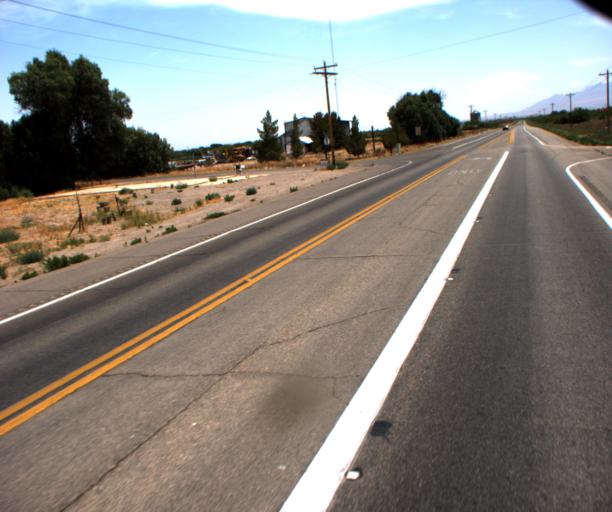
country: US
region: Arizona
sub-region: Graham County
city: Pima
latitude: 32.9622
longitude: -109.9205
